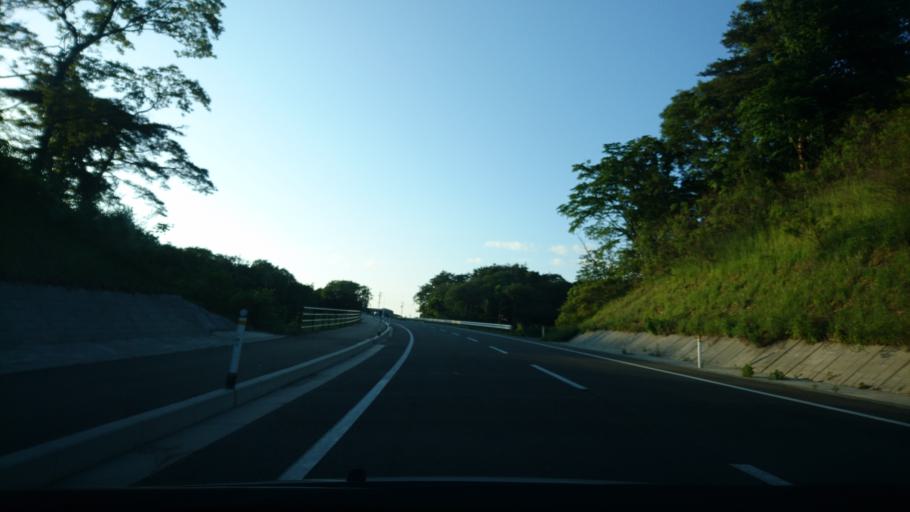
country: JP
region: Iwate
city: Ichinoseki
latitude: 38.8770
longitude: 141.1605
